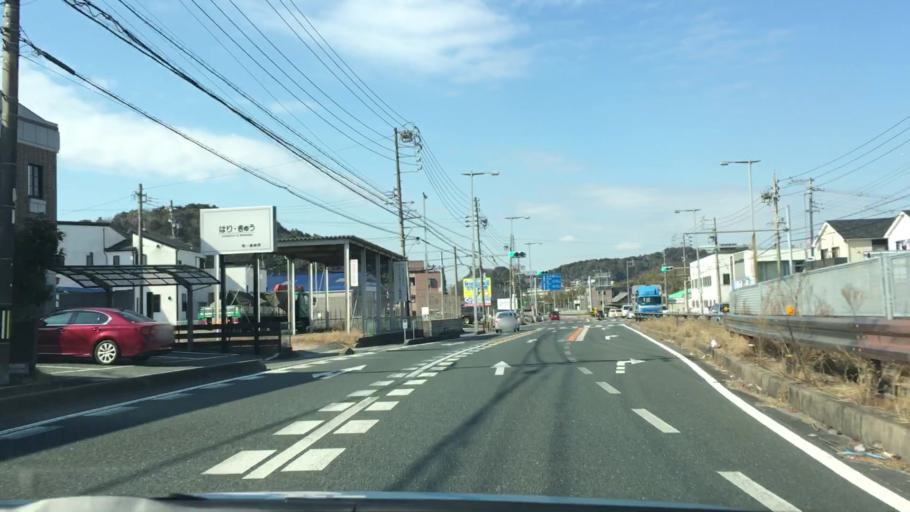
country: JP
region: Aichi
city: Gamagori
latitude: 34.8952
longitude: 137.2530
